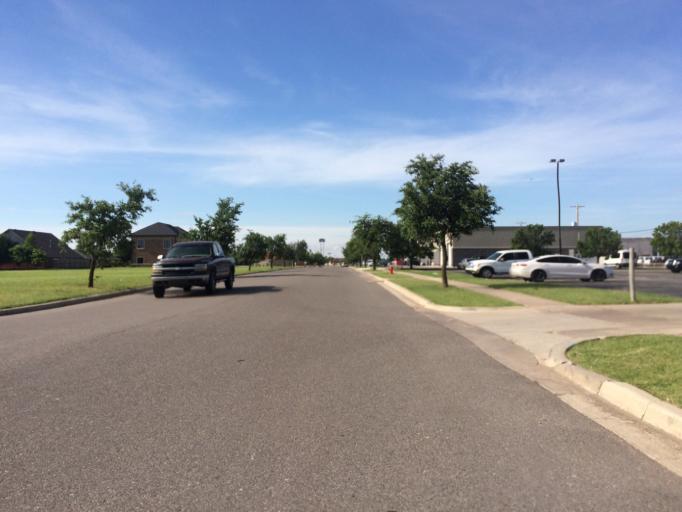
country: US
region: Oklahoma
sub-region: Cleveland County
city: Norman
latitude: 35.2289
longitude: -97.4829
